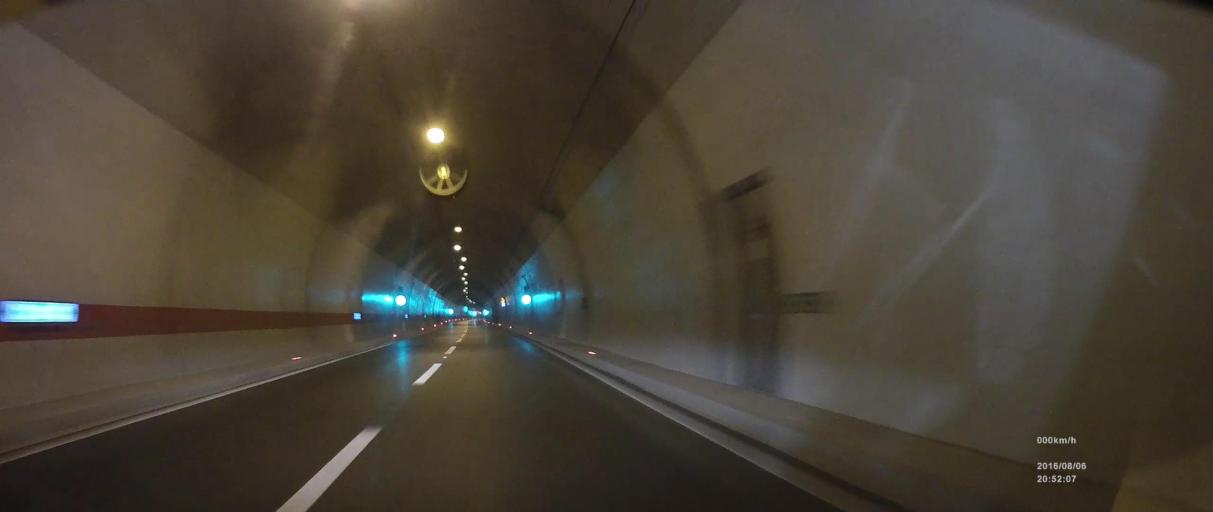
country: BA
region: Federation of Bosnia and Herzegovina
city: Ljubuski
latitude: 43.1245
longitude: 17.4851
